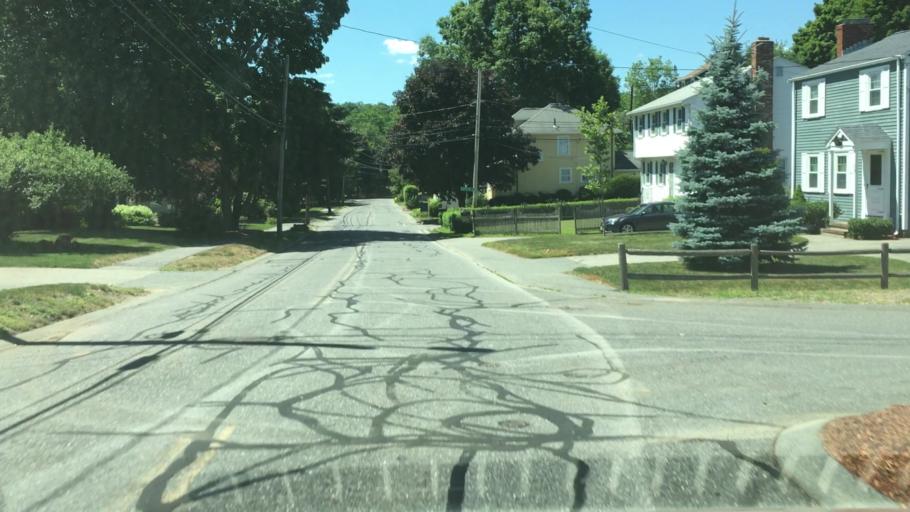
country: US
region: Massachusetts
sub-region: Middlesex County
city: Belmont
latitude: 42.4285
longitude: -71.1933
